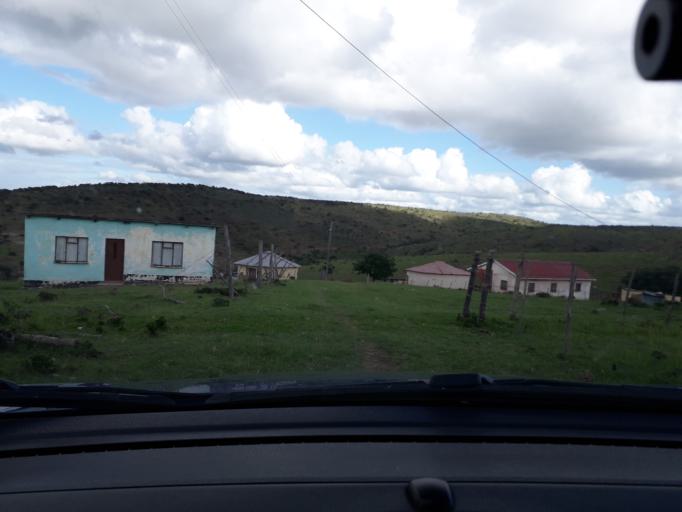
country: ZA
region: Eastern Cape
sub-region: Buffalo City Metropolitan Municipality
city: Bhisho
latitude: -33.1176
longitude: 27.4331
